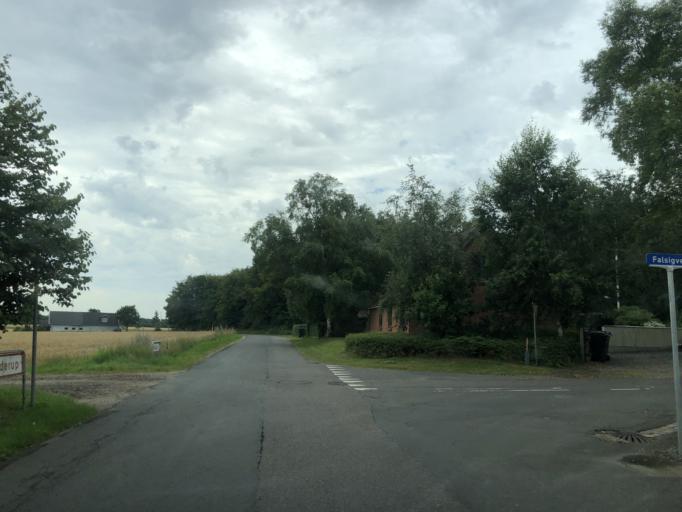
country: DK
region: Central Jutland
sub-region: Holstebro Kommune
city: Holstebro
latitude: 56.3854
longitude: 8.5215
